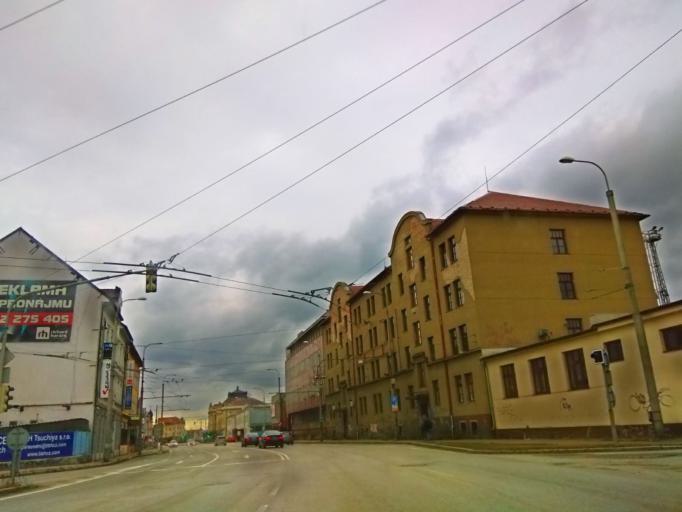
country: CZ
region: Jihocesky
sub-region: Okres Ceske Budejovice
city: Ceske Budejovice
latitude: 48.9716
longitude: 14.4890
